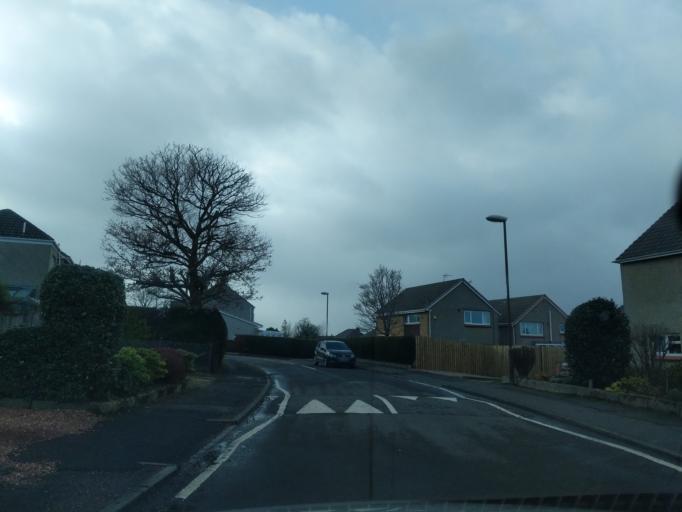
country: GB
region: Scotland
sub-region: Edinburgh
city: Currie
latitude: 55.9002
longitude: -3.2982
